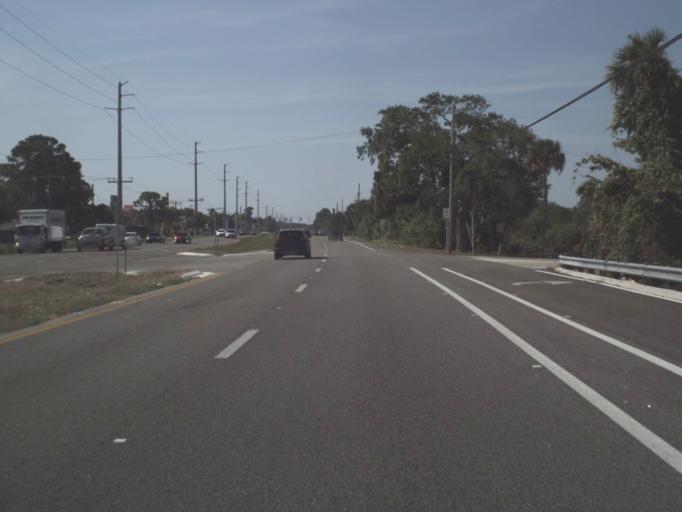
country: US
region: Florida
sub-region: Brevard County
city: Port Saint John
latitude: 28.4745
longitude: -80.7674
